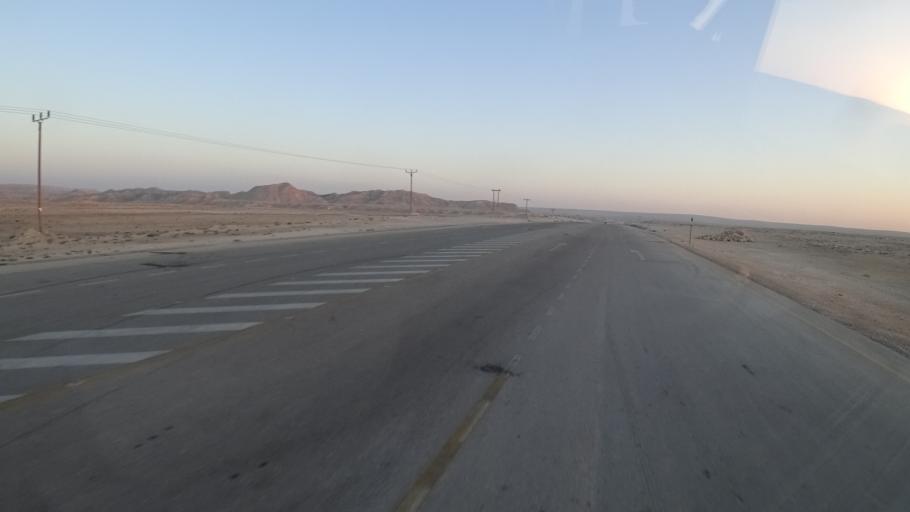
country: YE
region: Al Mahrah
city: Hawf
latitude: 16.9394
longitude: 53.3758
